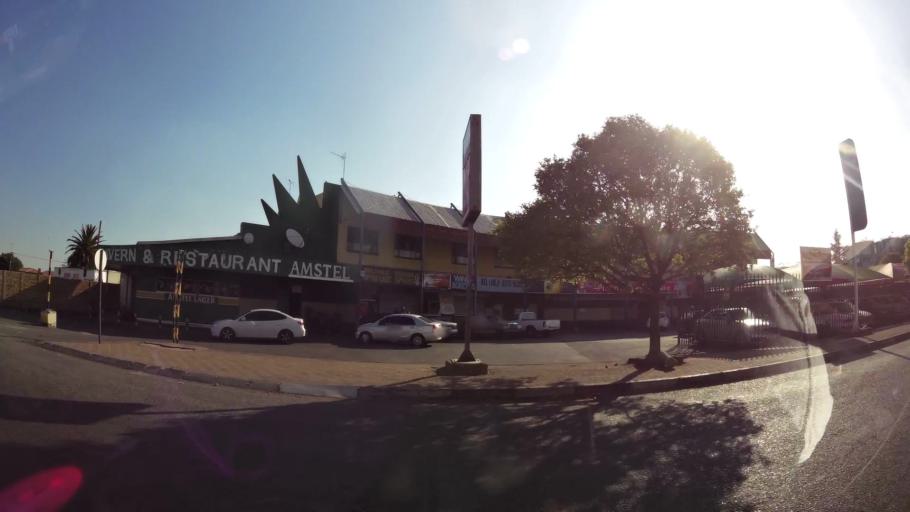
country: ZA
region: Gauteng
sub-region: West Rand District Municipality
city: Randfontein
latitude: -26.1660
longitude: 27.7122
